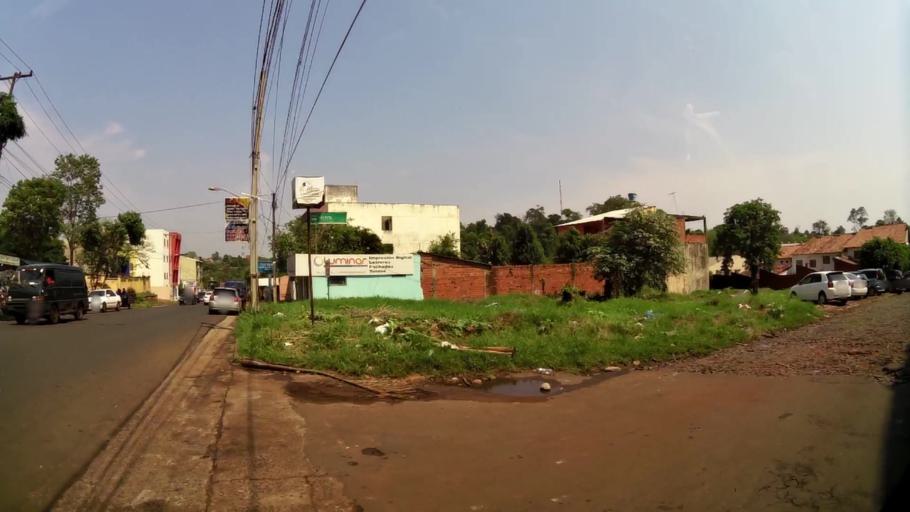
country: PY
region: Alto Parana
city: Presidente Franco
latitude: -25.5249
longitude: -54.6240
